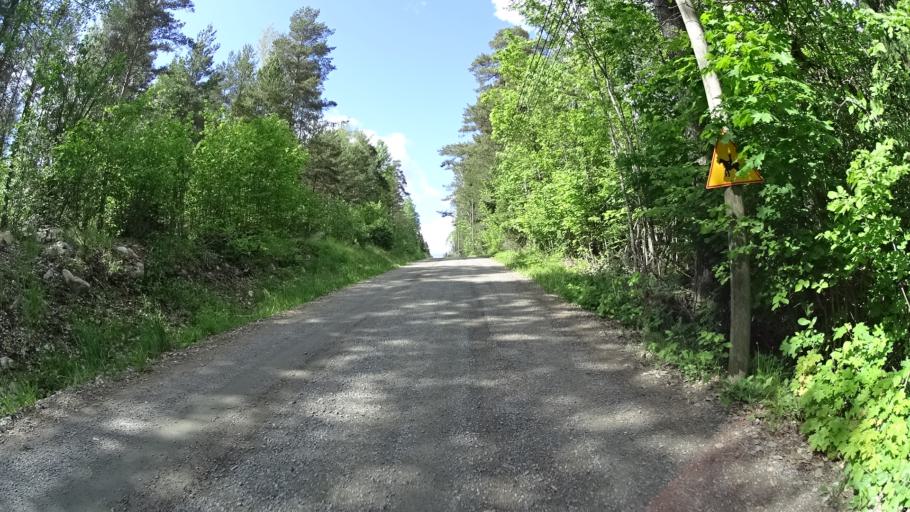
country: FI
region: Uusimaa
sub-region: Raaseporin
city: Pohja
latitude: 60.1709
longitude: 23.5887
